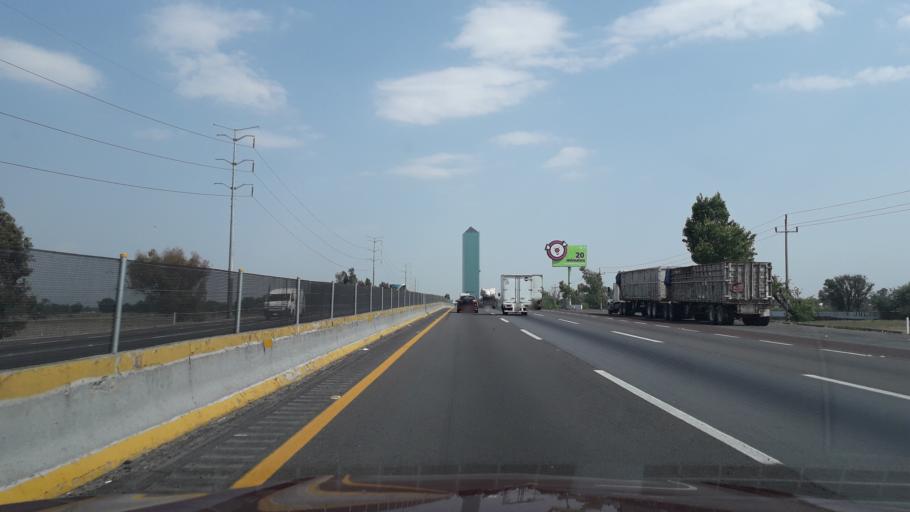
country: MX
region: Puebla
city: Santa Ana Xalmimilulco
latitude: 19.2357
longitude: -98.3808
